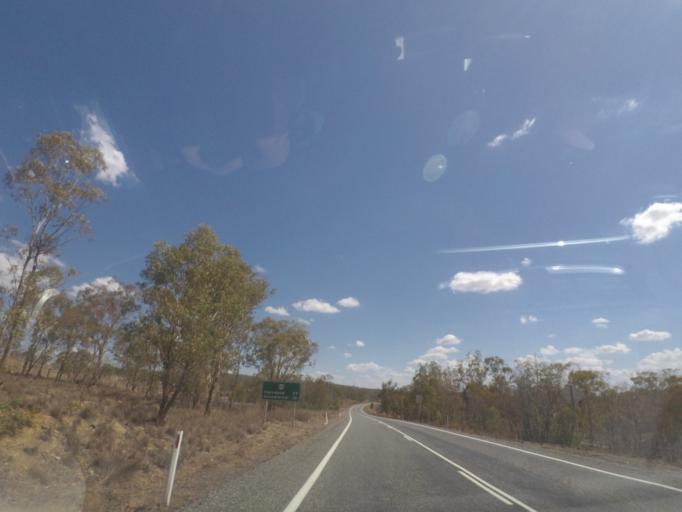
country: AU
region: Queensland
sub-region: Southern Downs
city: Warwick
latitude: -28.2109
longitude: 151.5646
